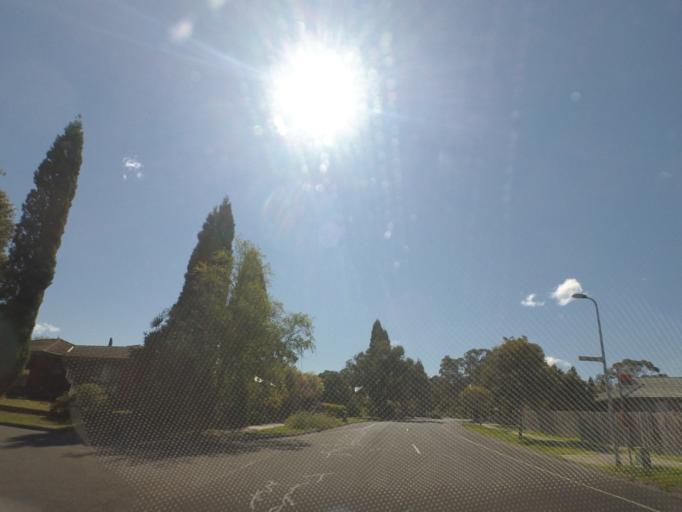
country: AU
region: Victoria
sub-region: Knox
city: Scoresby
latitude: -37.8966
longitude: 145.2203
